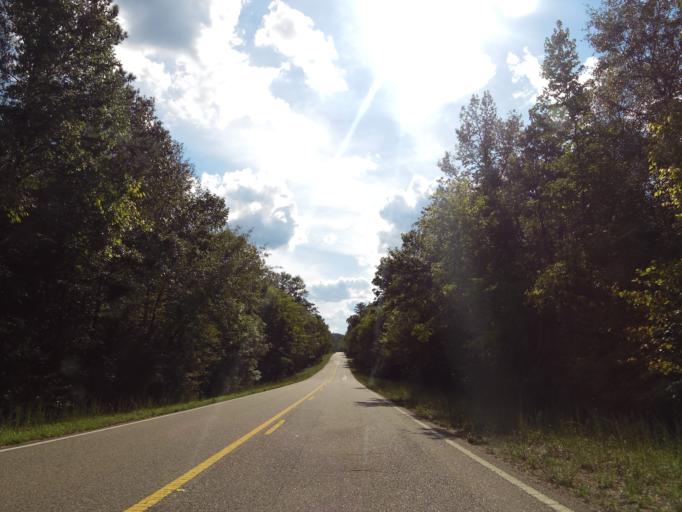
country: US
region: Alabama
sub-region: Dallas County
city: Selmont-West Selmont
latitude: 32.1839
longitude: -87.0403
